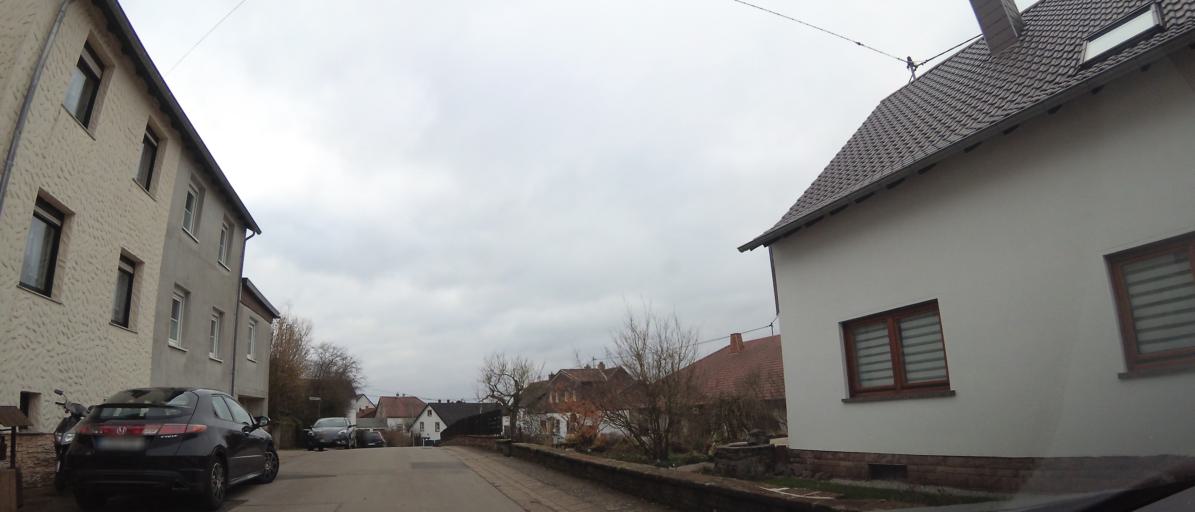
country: DE
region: Saarland
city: Illingen
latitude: 49.3890
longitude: 7.0777
